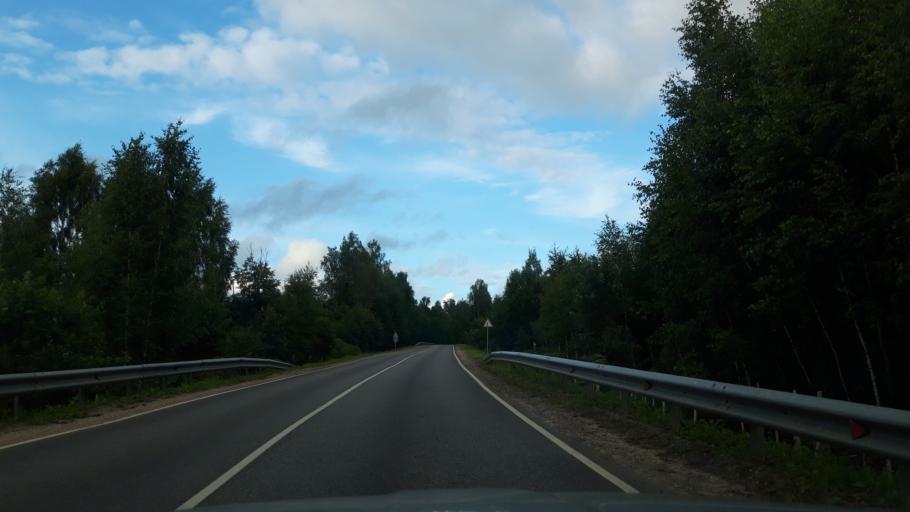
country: RU
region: Moskovskaya
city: Solnechnogorsk
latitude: 56.0953
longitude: 36.8463
